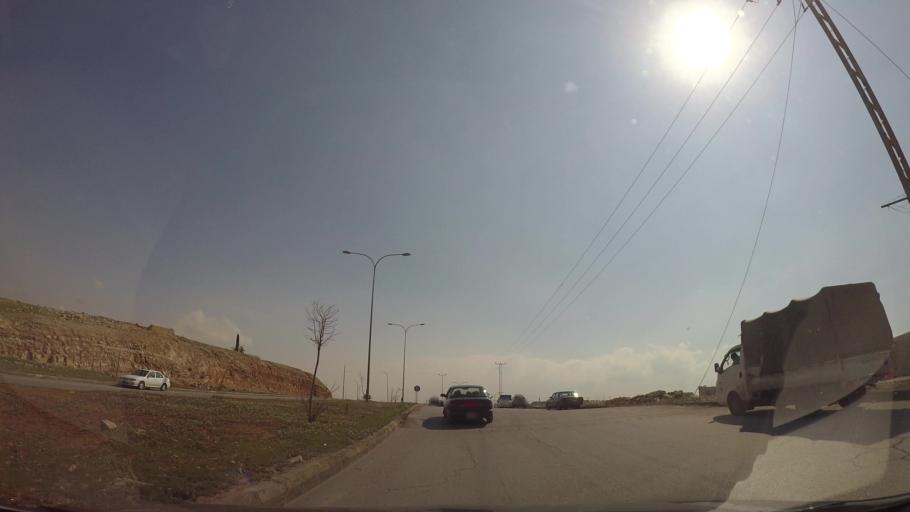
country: JO
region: Zarqa
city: Zarqa
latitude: 32.0747
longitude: 36.1033
